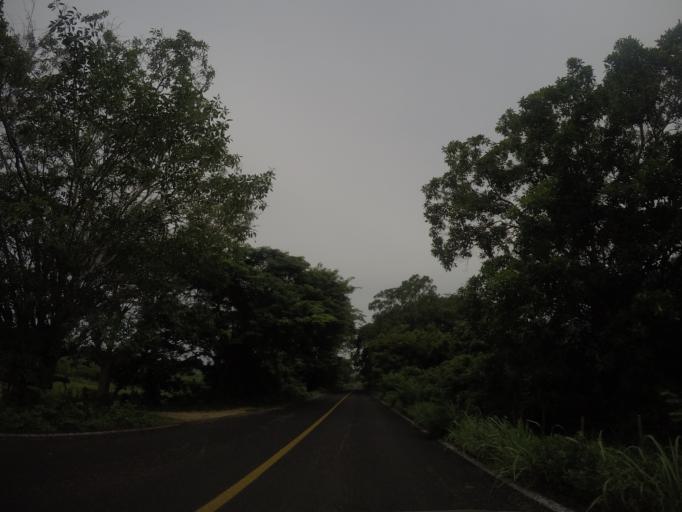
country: MX
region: Oaxaca
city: San Pedro Mixtepec
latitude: 15.9572
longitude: -97.2431
